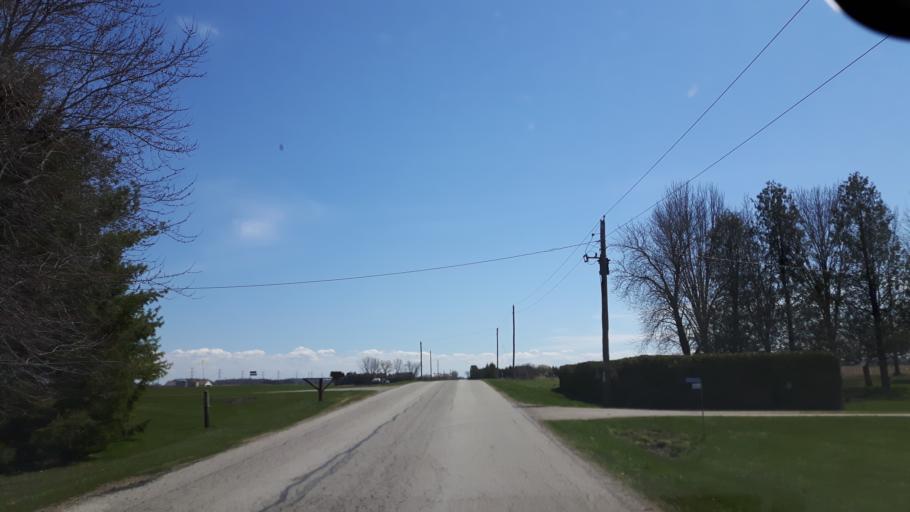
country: CA
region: Ontario
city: Goderich
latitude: 43.6262
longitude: -81.6440
